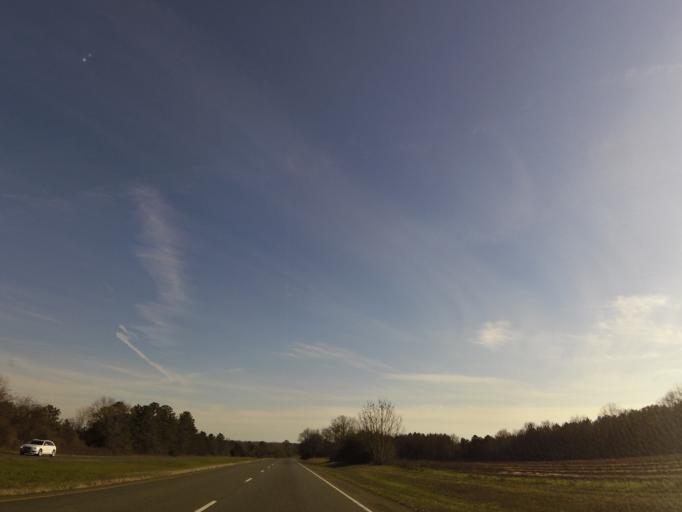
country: US
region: Georgia
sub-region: Stewart County
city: Richland
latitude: 32.1244
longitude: -84.6803
